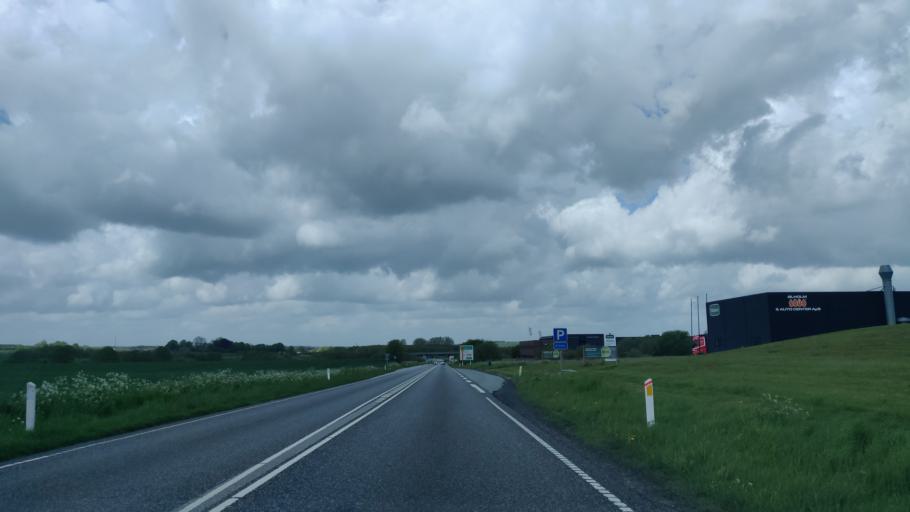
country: DK
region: Central Jutland
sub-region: Hedensted Kommune
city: Torring
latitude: 55.8341
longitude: 9.5140
